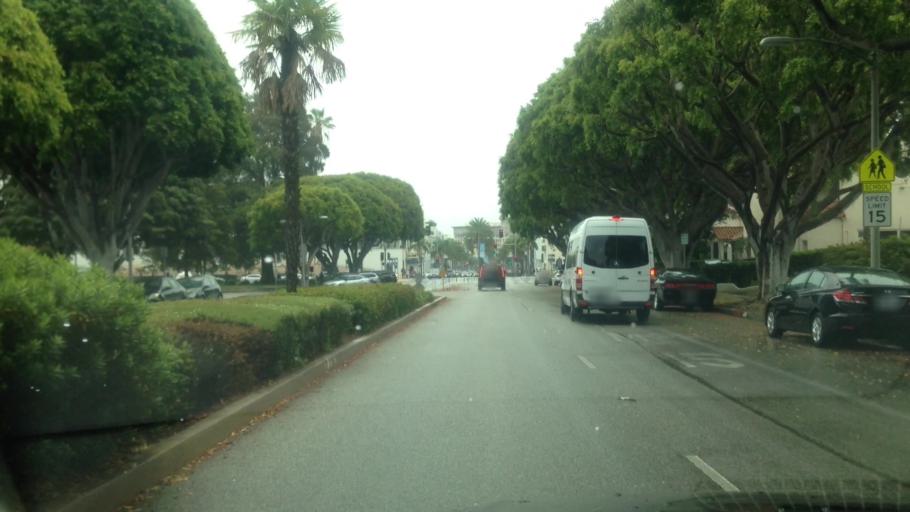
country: US
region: California
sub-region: Los Angeles County
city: Beverly Hills
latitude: 34.0720
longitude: -118.4058
